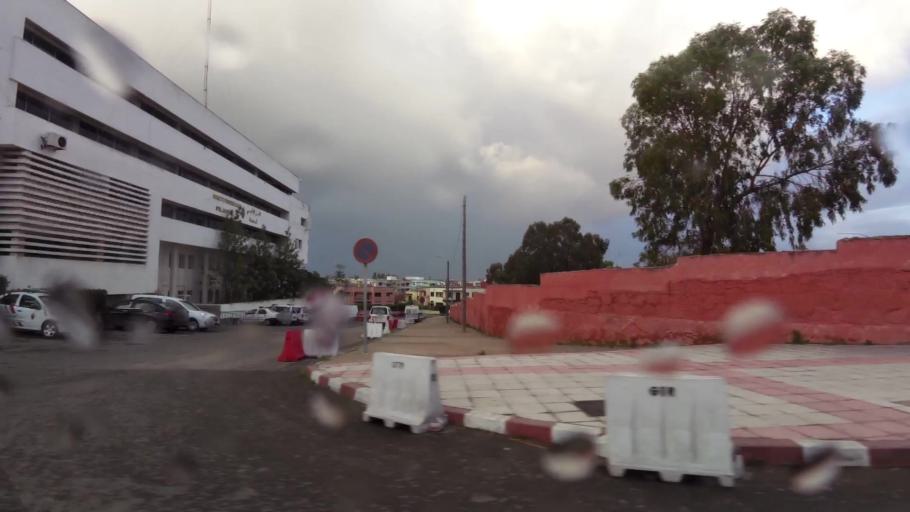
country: MA
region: Doukkala-Abda
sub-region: El-Jadida
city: El Jadida
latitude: 33.2425
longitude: -8.5040
